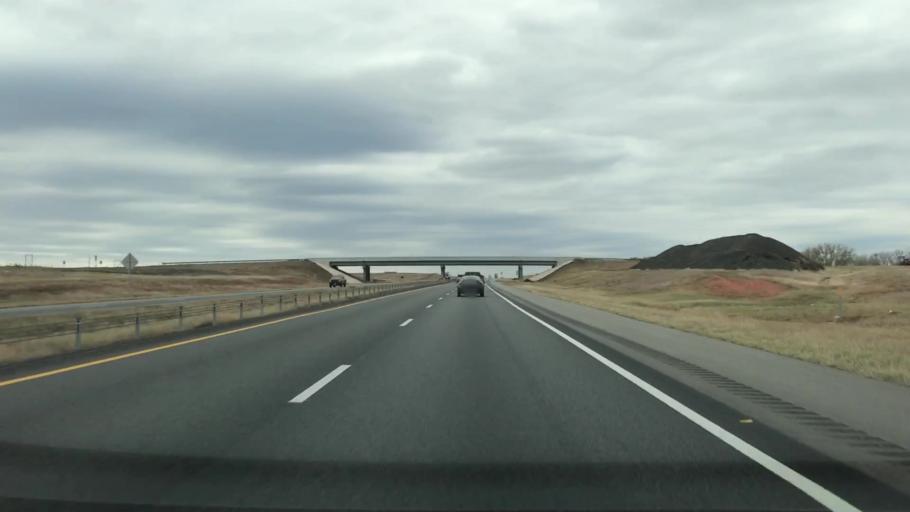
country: US
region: Oklahoma
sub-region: Beckham County
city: Elk City
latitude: 35.3860
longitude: -99.4673
